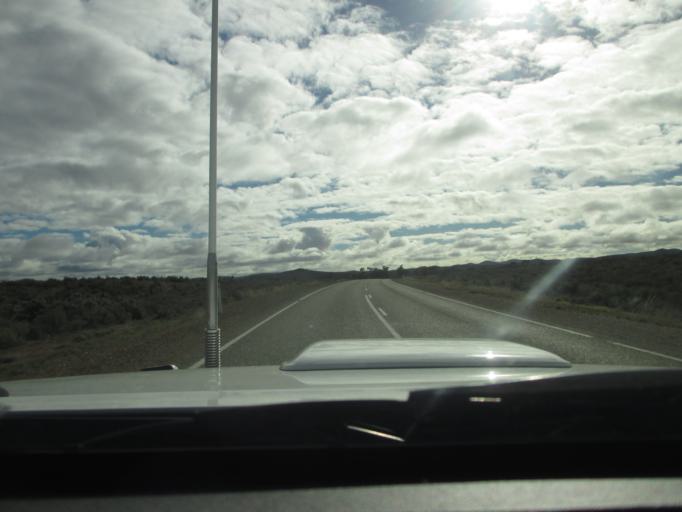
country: AU
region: South Australia
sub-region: Flinders Ranges
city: Quorn
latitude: -32.2883
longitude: 138.4922
